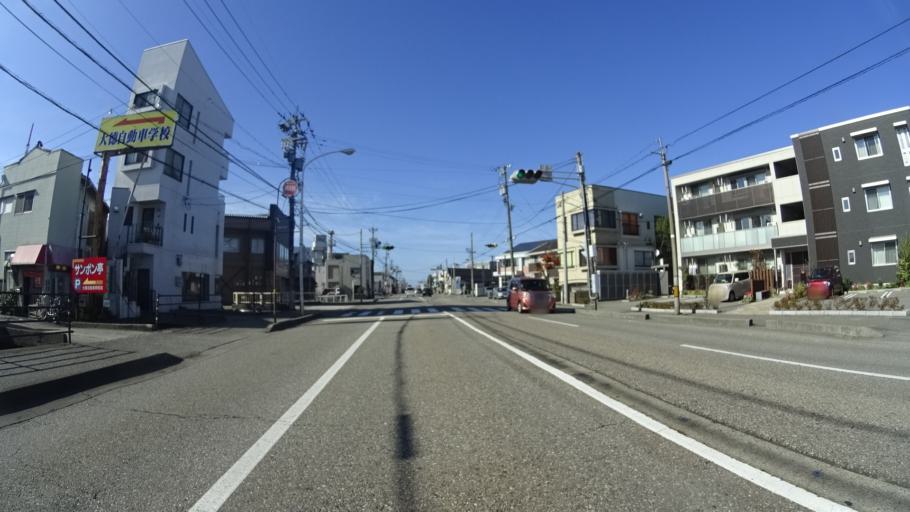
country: JP
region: Ishikawa
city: Kanazawa-shi
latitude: 36.5911
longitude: 136.6128
